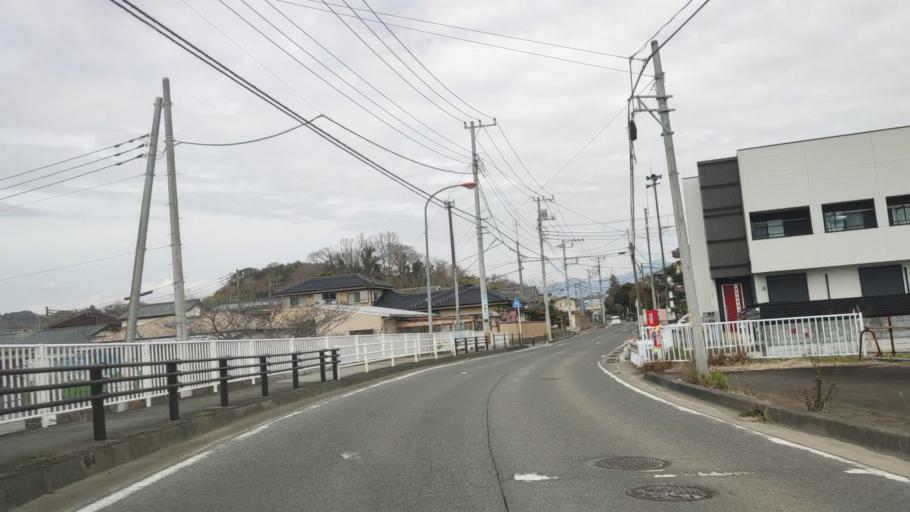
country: JP
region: Kanagawa
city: Ninomiya
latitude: 35.3027
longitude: 139.2268
